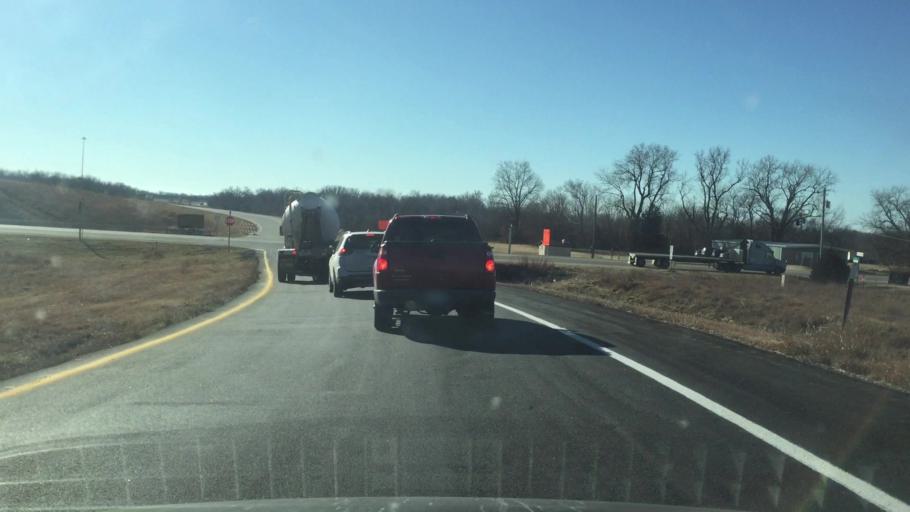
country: US
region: Kansas
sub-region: Allen County
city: Iola
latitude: 37.9231
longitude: -95.3803
